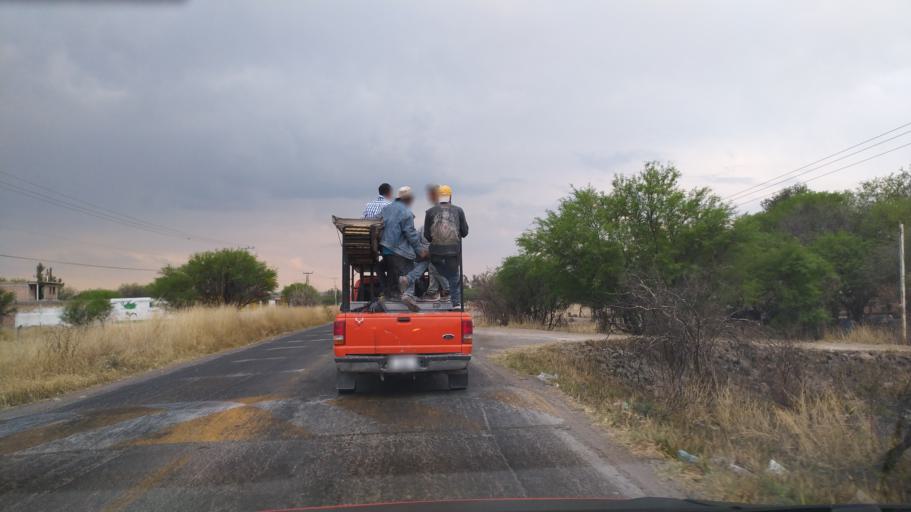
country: MX
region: Guanajuato
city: Ciudad Manuel Doblado
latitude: 20.7988
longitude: -101.9057
